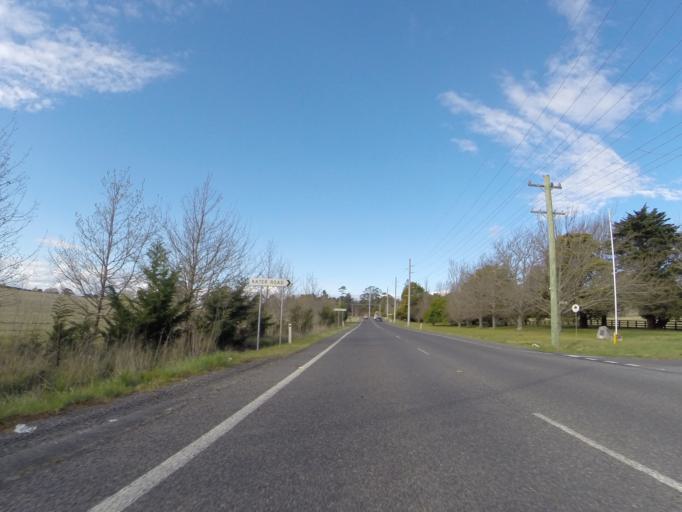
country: AU
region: New South Wales
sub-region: Wingecarribee
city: Moss Vale
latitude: -34.5623
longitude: 150.3405
